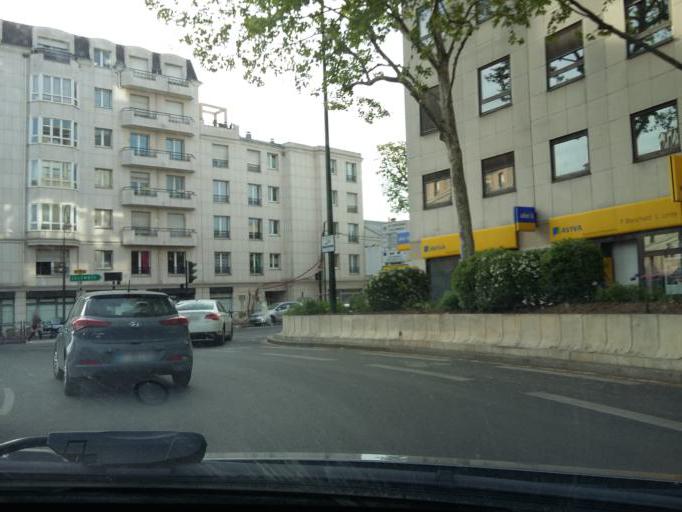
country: FR
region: Ile-de-France
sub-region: Departement des Hauts-de-Seine
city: Courbevoie
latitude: 48.9056
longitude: 2.2561
